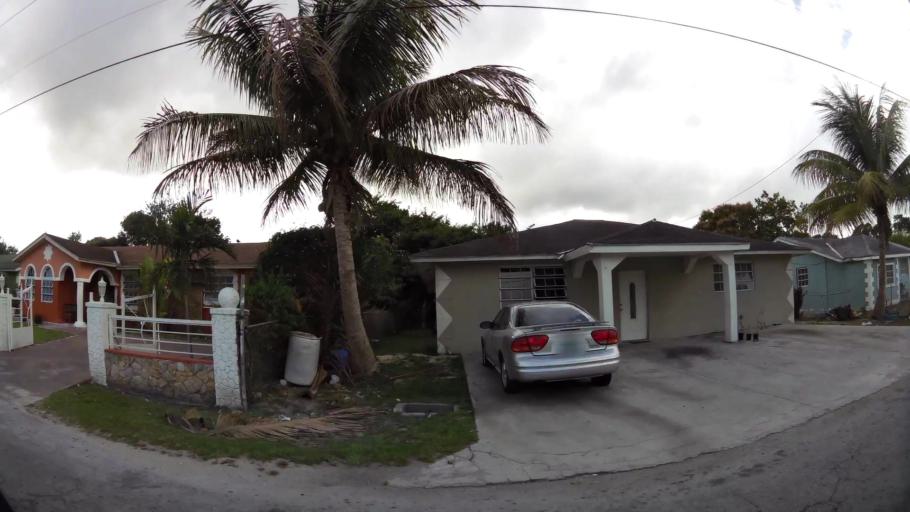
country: BS
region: Freeport
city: Freeport
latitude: 26.5312
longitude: -78.7022
